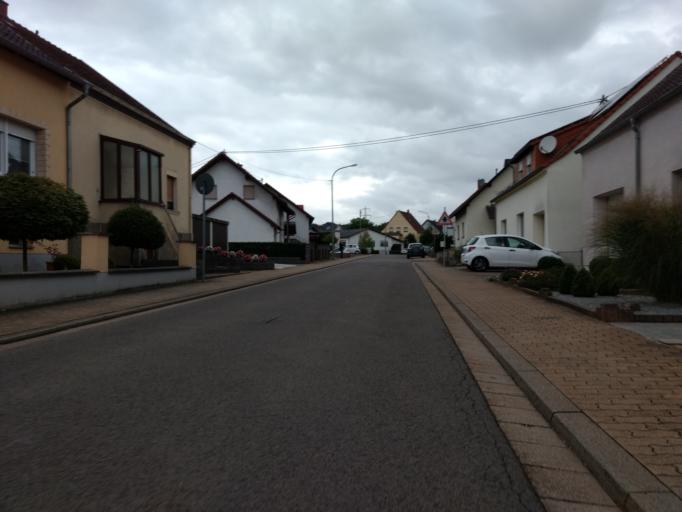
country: DE
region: Saarland
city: Nalbach
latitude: 49.3747
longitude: 6.7582
